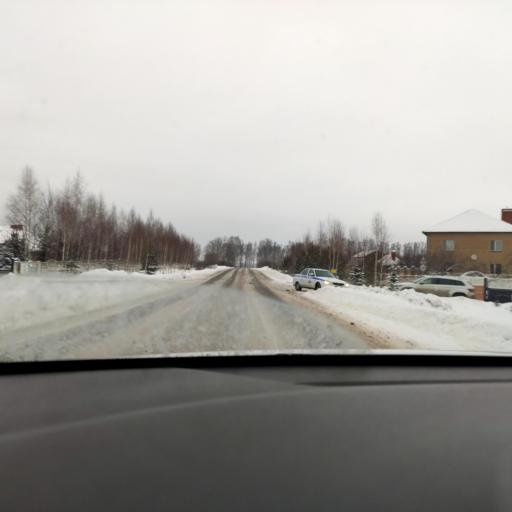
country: RU
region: Tatarstan
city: Osinovo
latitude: 55.8580
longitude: 48.8208
